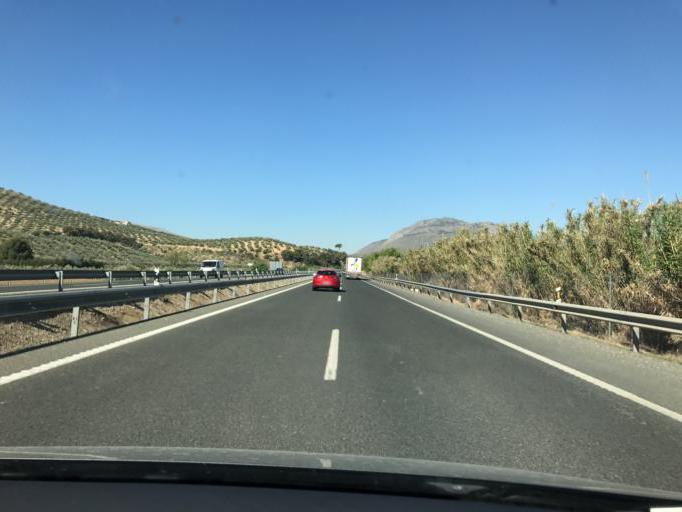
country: ES
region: Andalusia
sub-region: Provincia de Granada
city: Huetor-Tajar
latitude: 37.1803
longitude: -4.0648
